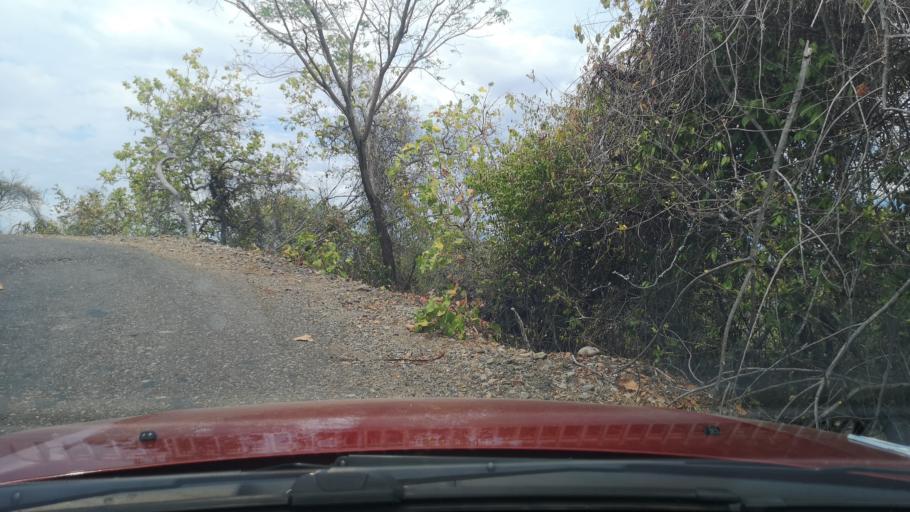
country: CO
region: Huila
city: Neiva
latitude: 2.9559
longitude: -75.3443
